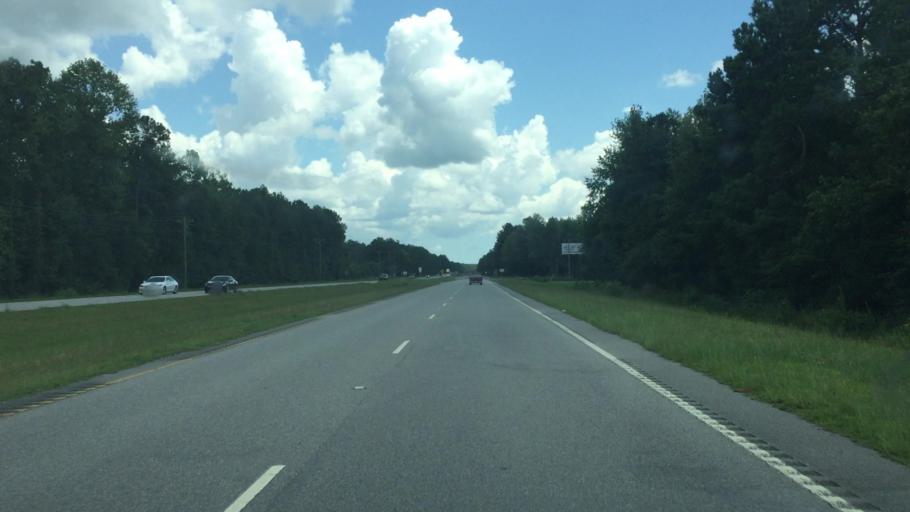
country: US
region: South Carolina
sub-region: Horry County
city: Loris
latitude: 34.0421
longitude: -78.8240
